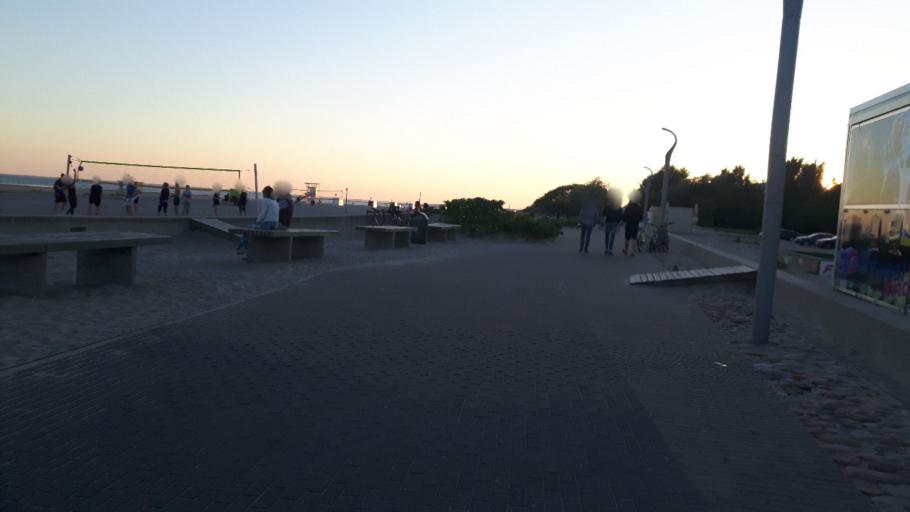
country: EE
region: Paernumaa
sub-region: Paernu linn
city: Parnu
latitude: 58.3719
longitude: 24.5073
